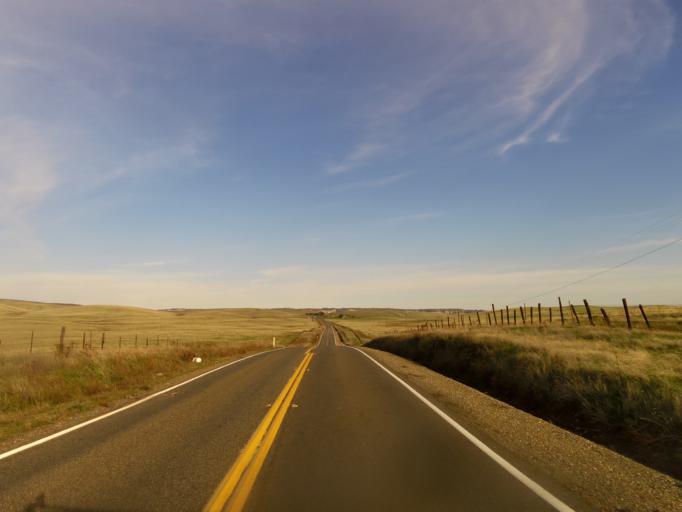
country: US
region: California
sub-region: El Dorado County
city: El Dorado Hills
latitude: 38.6229
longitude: -121.1097
